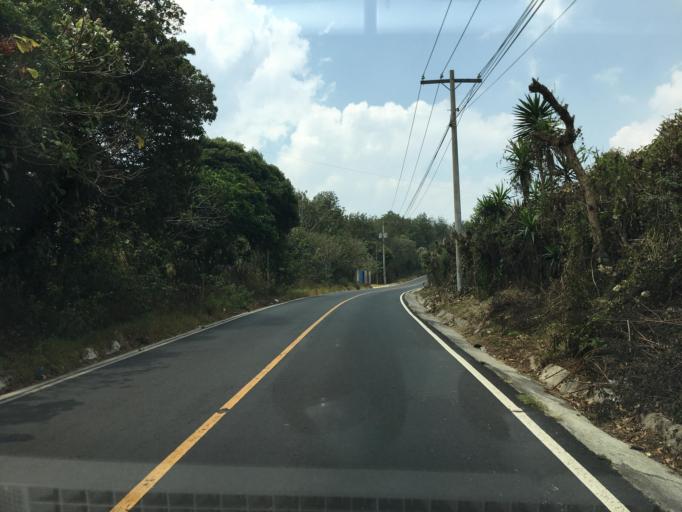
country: GT
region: Guatemala
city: Villa Canales
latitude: 14.4095
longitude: -90.5363
